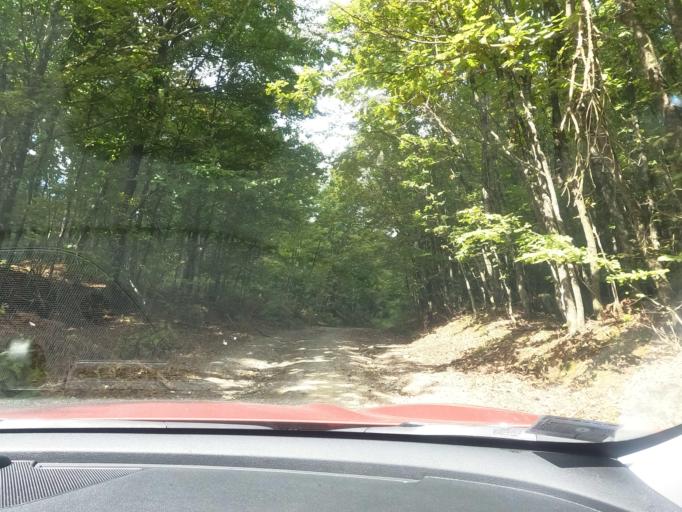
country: BA
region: Federation of Bosnia and Herzegovina
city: Velika Kladusa
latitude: 45.2546
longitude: 15.7909
